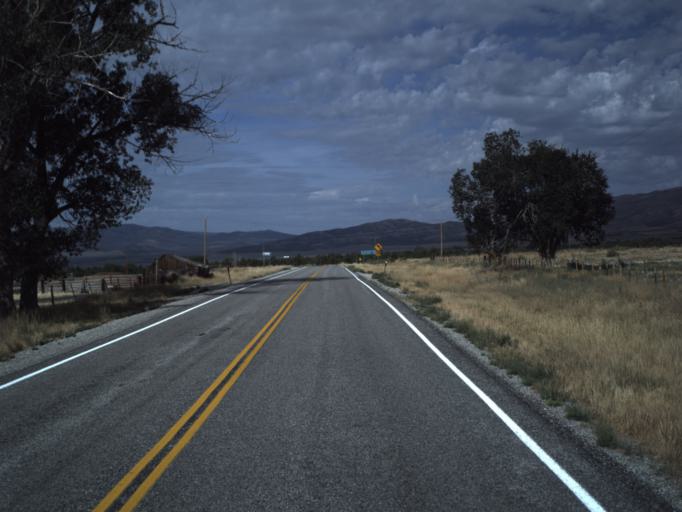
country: US
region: Idaho
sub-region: Cassia County
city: Burley
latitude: 41.8201
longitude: -113.4247
